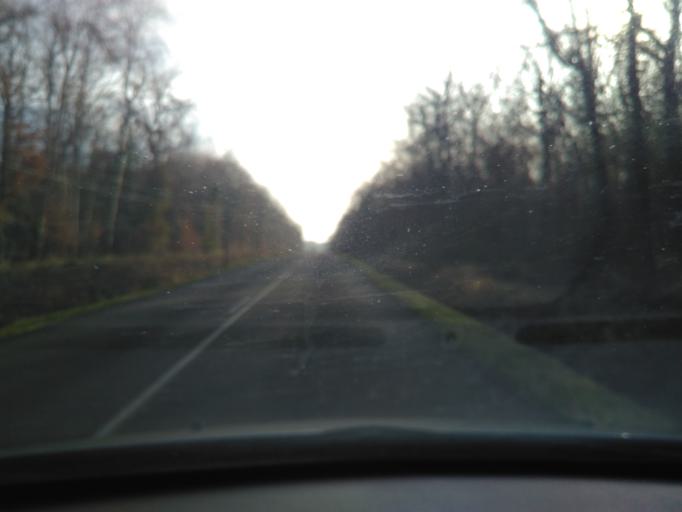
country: FR
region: Bourgogne
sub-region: Departement de la Nievre
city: Dornes
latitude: 46.7859
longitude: 3.2758
